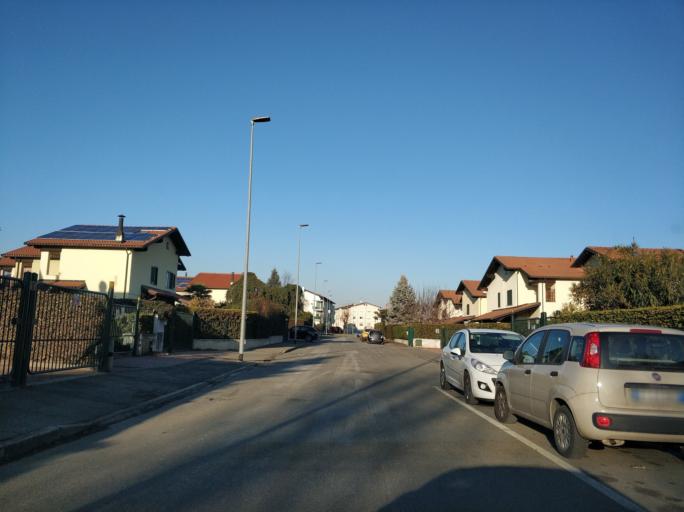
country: IT
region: Piedmont
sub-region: Provincia di Torino
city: San Maurizio
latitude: 45.2114
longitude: 7.6250
